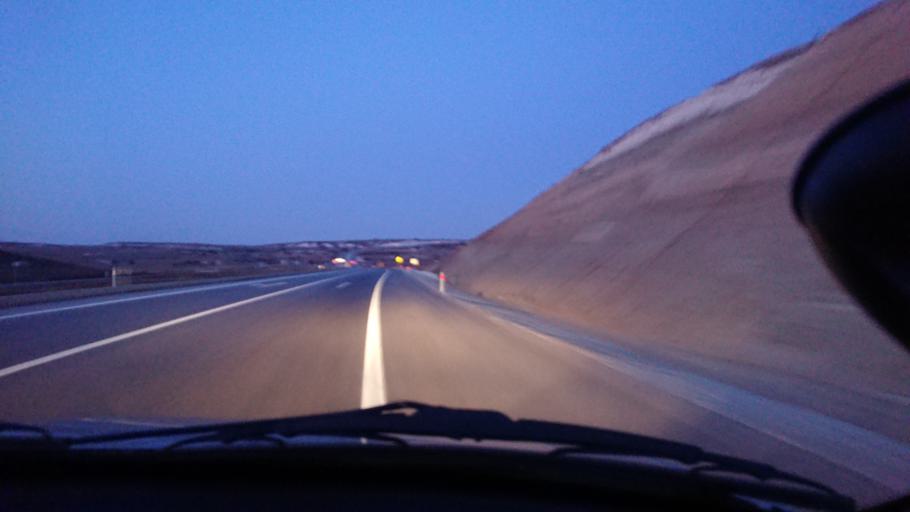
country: TR
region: Kuetahya
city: Cavdarhisar
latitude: 39.1315
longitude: 29.5508
